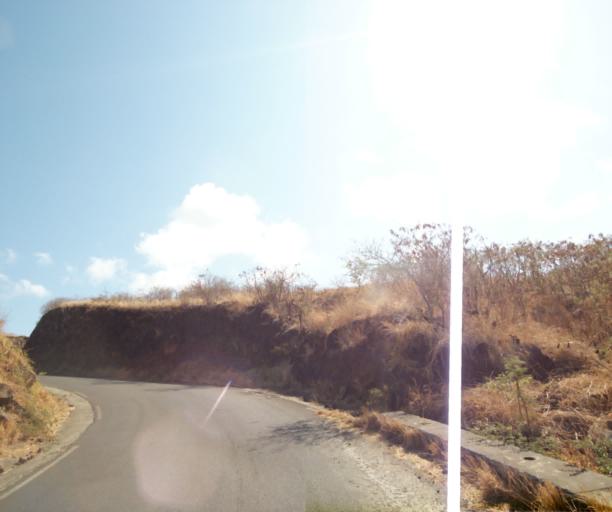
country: RE
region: Reunion
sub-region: Reunion
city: Trois-Bassins
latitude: -21.1031
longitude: 55.2501
